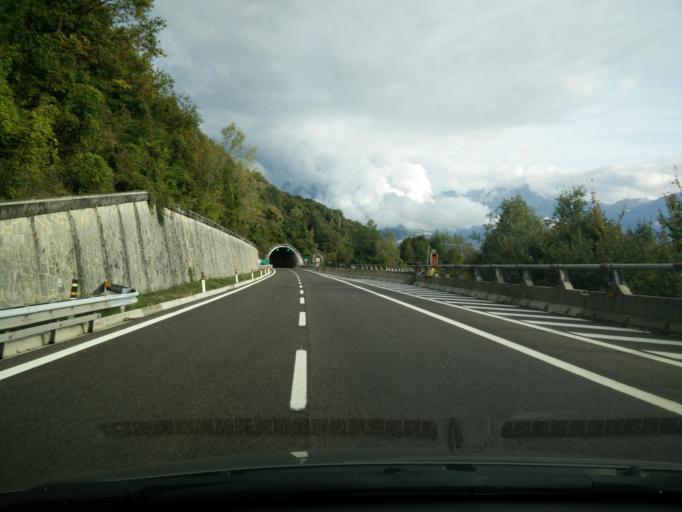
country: IT
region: Veneto
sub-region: Provincia di Belluno
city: Farra d'Alpago
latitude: 46.0991
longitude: 12.3247
